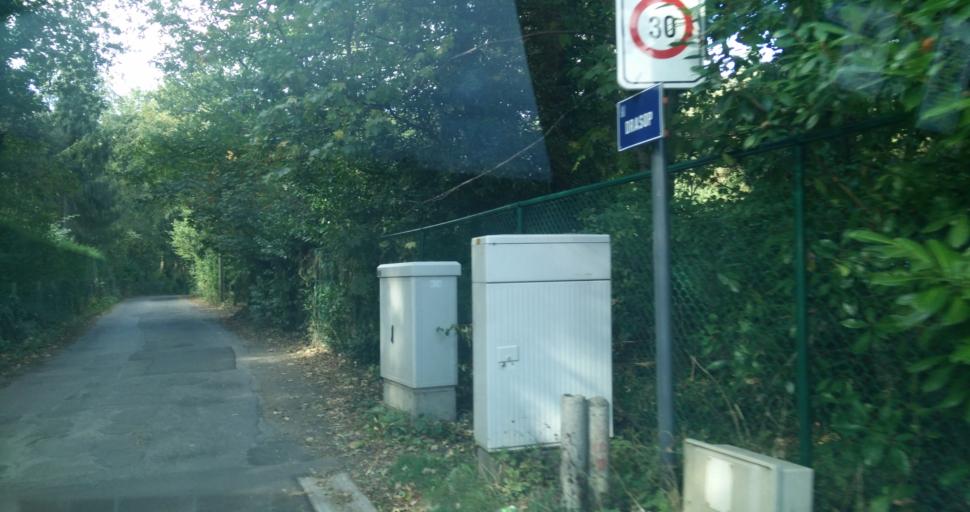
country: BE
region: Flanders
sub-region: Provincie Vlaams-Brabant
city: Halle
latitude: 50.7256
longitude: 4.2740
